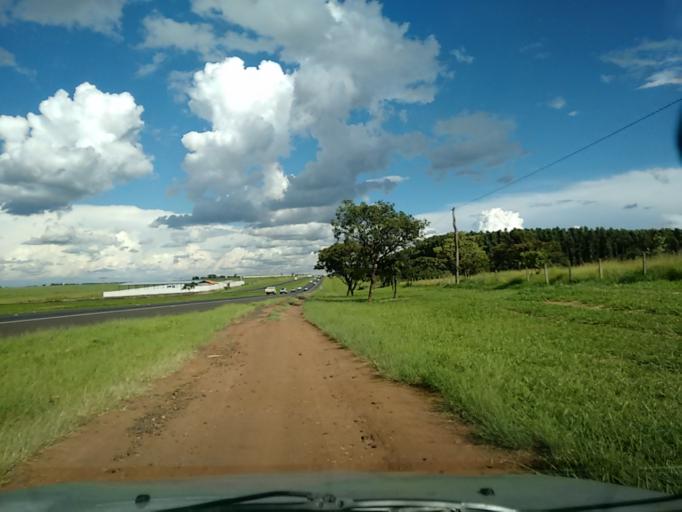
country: BR
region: Sao Paulo
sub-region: Ibate
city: Ibate
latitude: -21.9235
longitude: -48.0308
